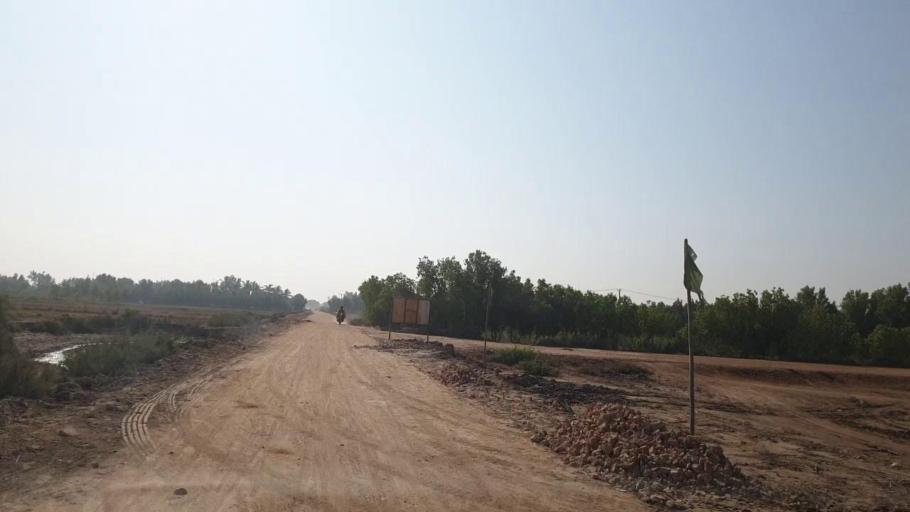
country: PK
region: Sindh
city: Thatta
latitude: 24.7653
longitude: 67.9139
